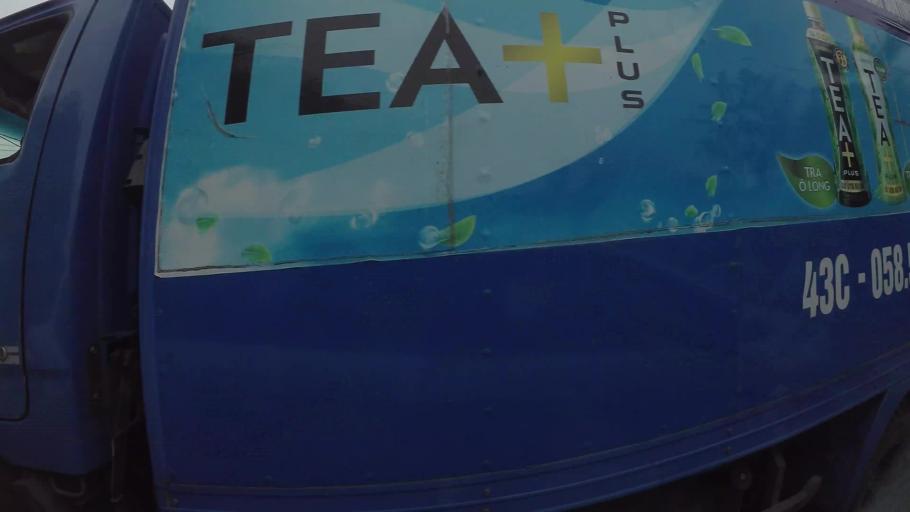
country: VN
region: Da Nang
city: Thanh Khe
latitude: 16.0668
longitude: 108.1781
